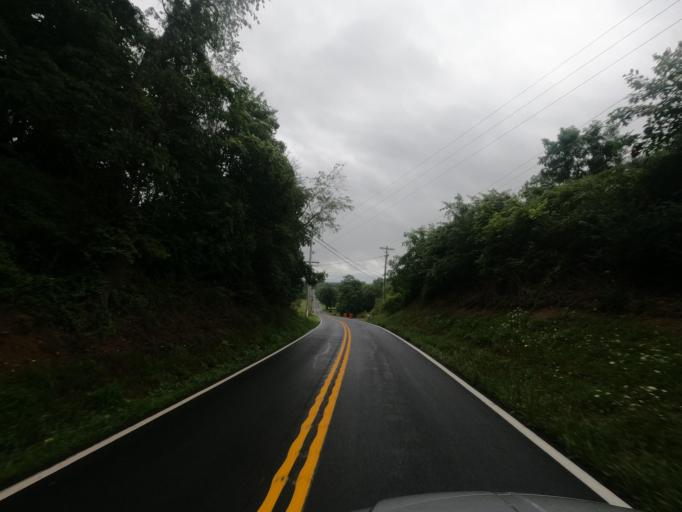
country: US
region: Maryland
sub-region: Washington County
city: Wilson-Conococheague
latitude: 39.6244
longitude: -77.9640
